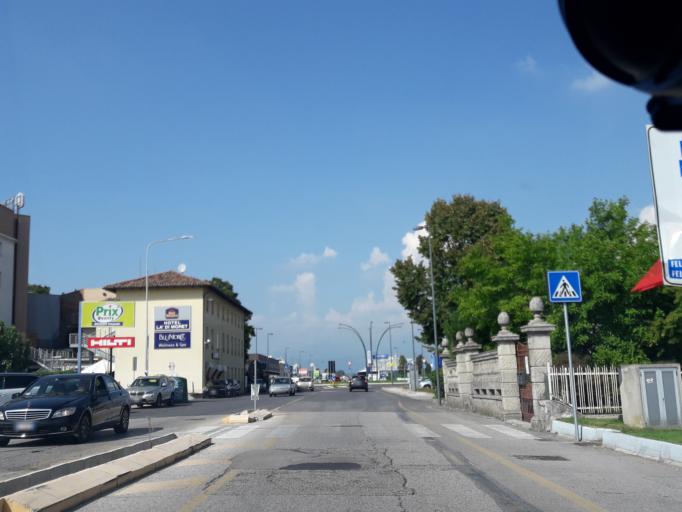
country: IT
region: Friuli Venezia Giulia
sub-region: Provincia di Udine
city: Feletto Umberto
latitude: 46.0971
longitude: 13.2308
